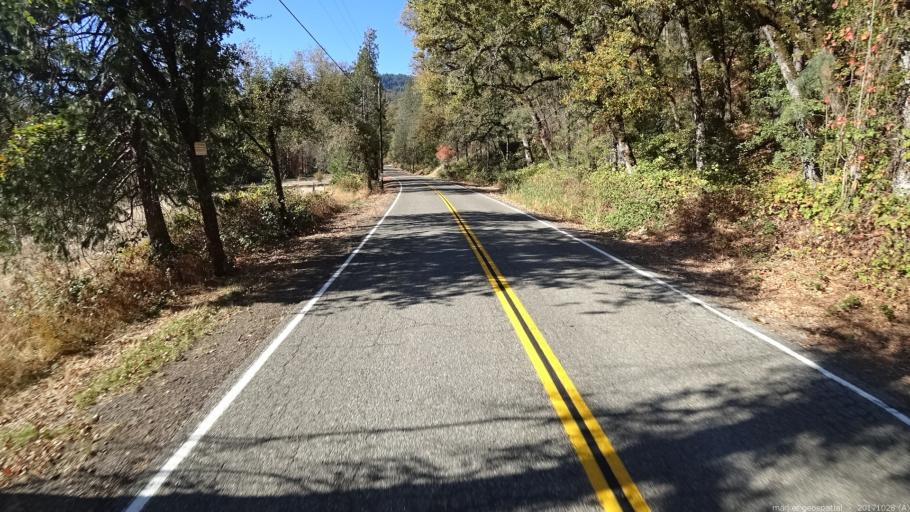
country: US
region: California
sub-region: Trinity County
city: Lewiston
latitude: 40.7484
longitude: -122.6221
